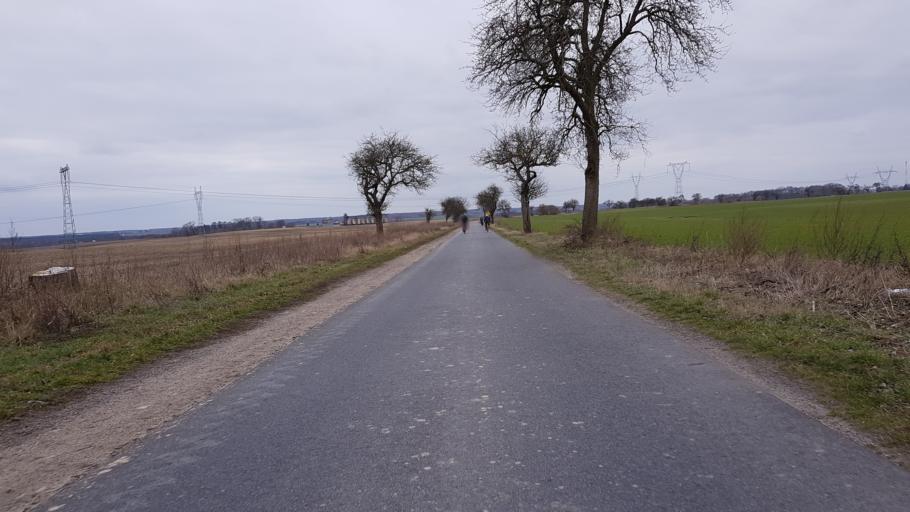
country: PL
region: West Pomeranian Voivodeship
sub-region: Powiat gryfinski
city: Banie
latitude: 53.0971
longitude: 14.6894
